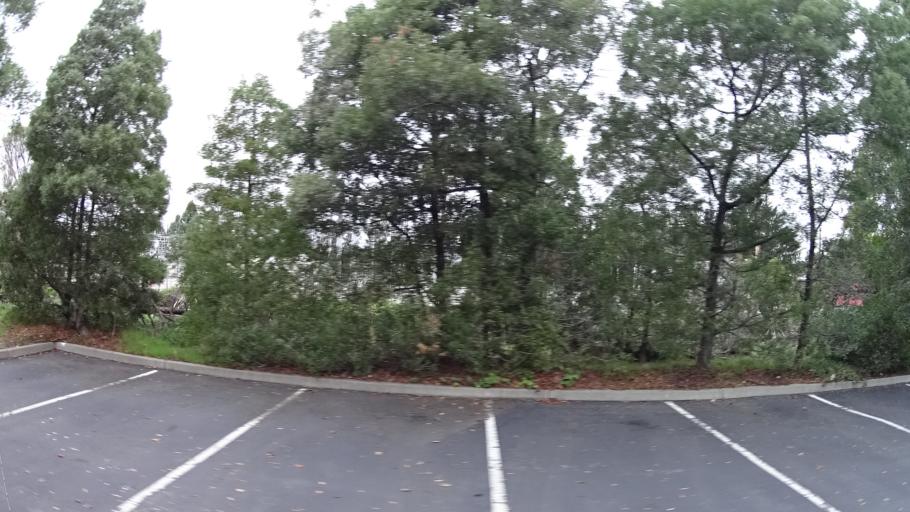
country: US
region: California
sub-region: San Mateo County
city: Foster City
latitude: 37.5513
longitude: -122.2920
